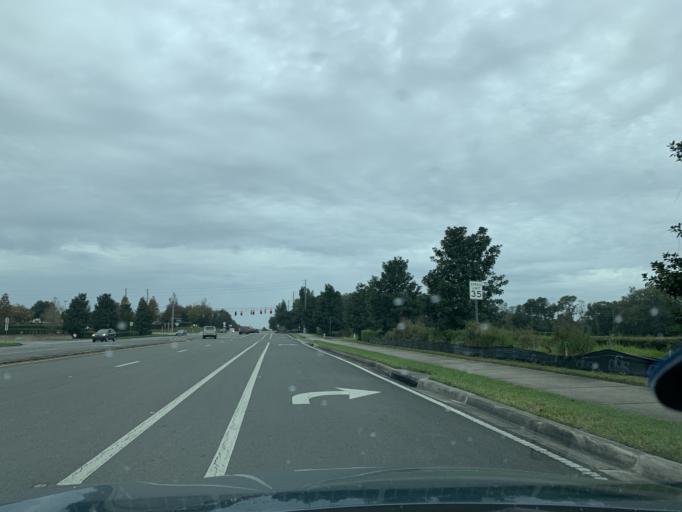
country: US
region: Florida
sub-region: Pasco County
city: Zephyrhills North
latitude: 28.2737
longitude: -82.1864
